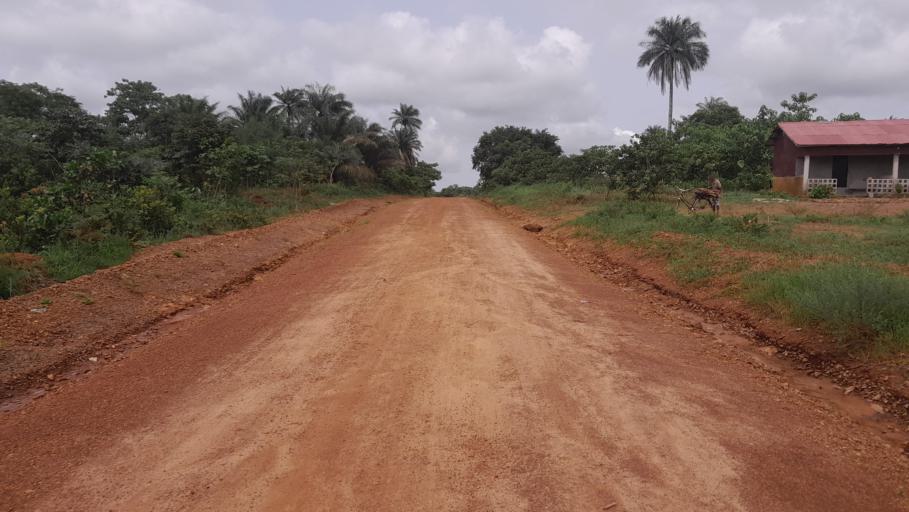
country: GN
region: Boke
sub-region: Boffa
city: Boffa
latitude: 10.0967
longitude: -13.8565
